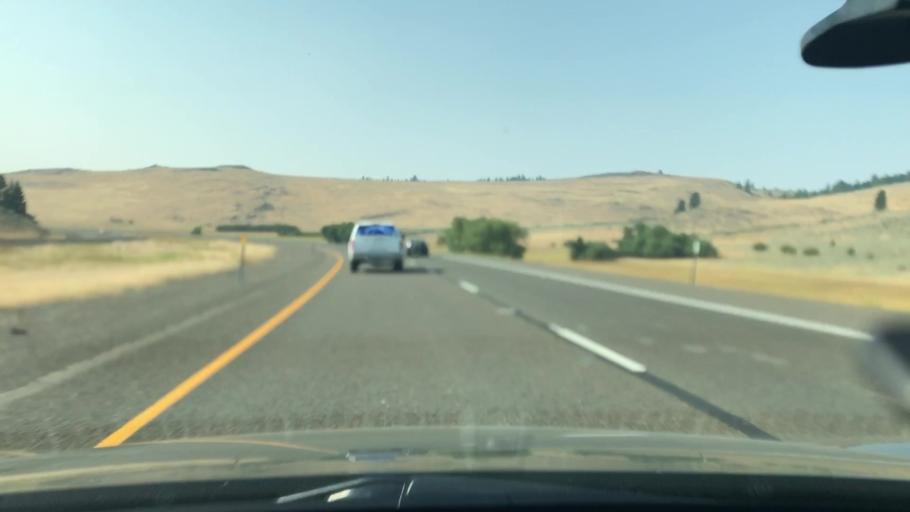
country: US
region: Oregon
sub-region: Union County
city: Union
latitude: 45.1669
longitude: -117.9649
